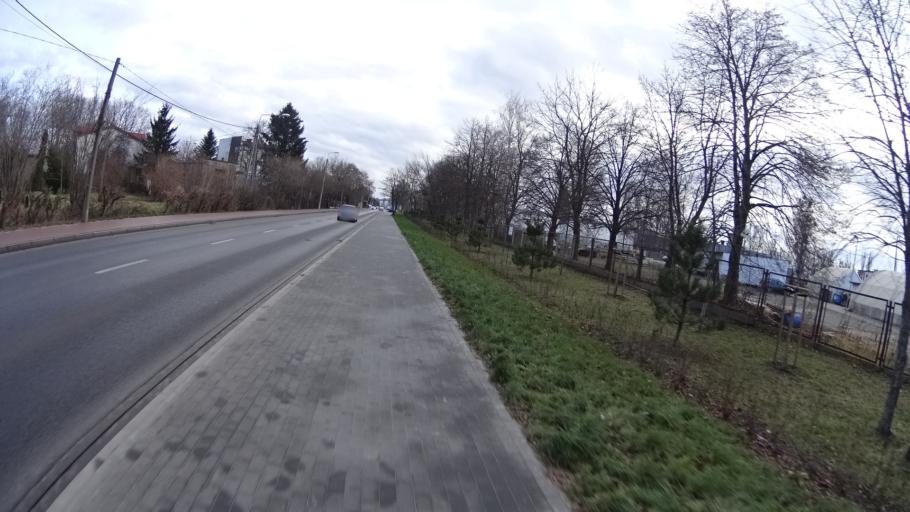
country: PL
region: Masovian Voivodeship
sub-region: Powiat pruszkowski
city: Pruszkow
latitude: 52.1671
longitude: 20.7771
